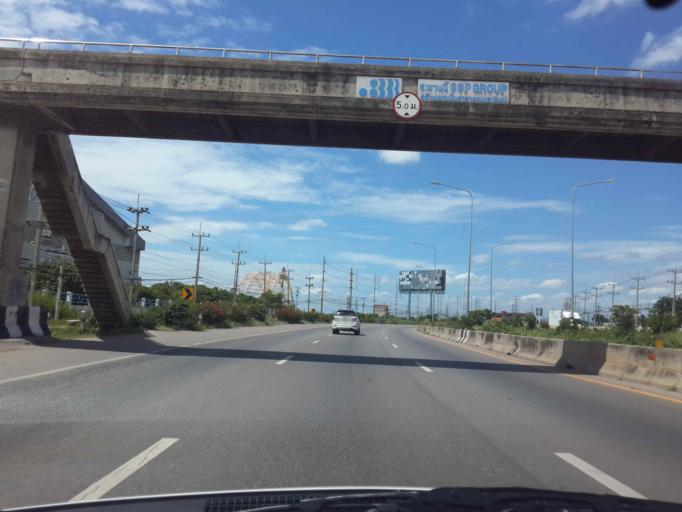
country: TH
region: Samut Sakhon
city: Ban Phaeo
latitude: 13.5034
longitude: 100.1266
